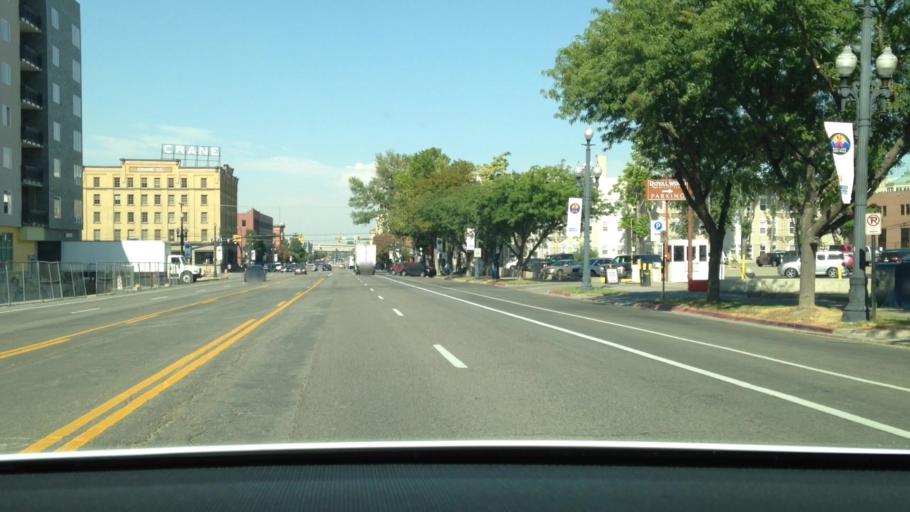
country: US
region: Utah
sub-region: Salt Lake County
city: Salt Lake City
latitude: 40.7651
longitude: -111.8977
